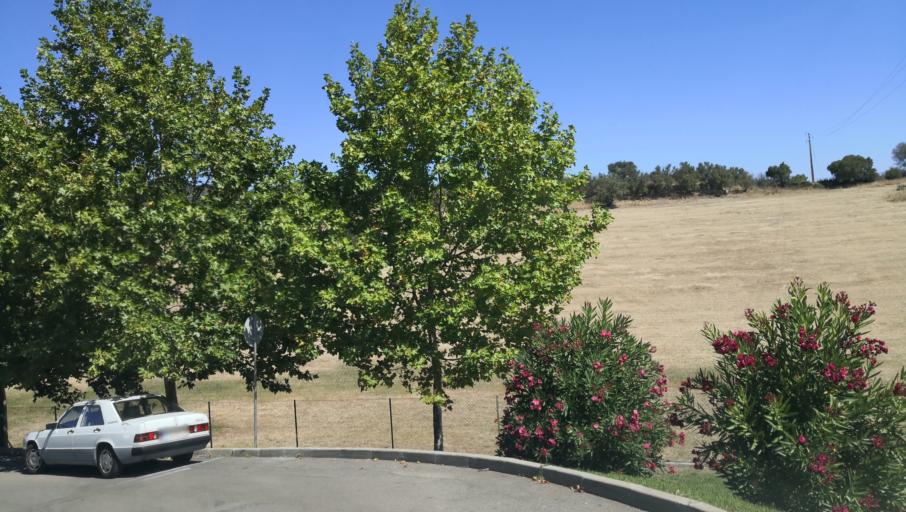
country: PT
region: Setubal
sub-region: Setubal
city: Setubal
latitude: 38.5335
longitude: -8.9088
